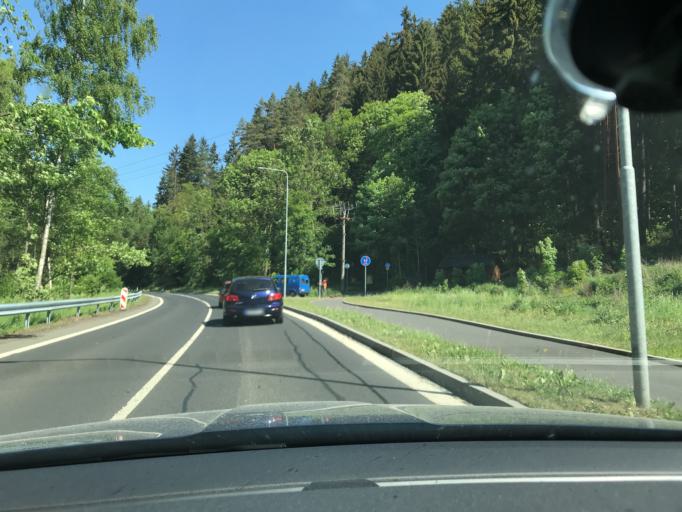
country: CZ
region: Karlovarsky
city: Jachymov
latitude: 50.3391
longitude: 12.9390
